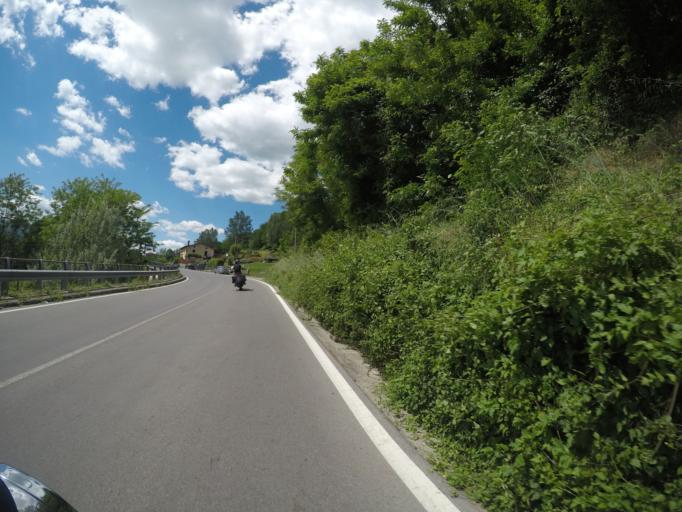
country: IT
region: Tuscany
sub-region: Provincia di Lucca
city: Villa Collemandina
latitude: 44.1388
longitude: 10.3808
